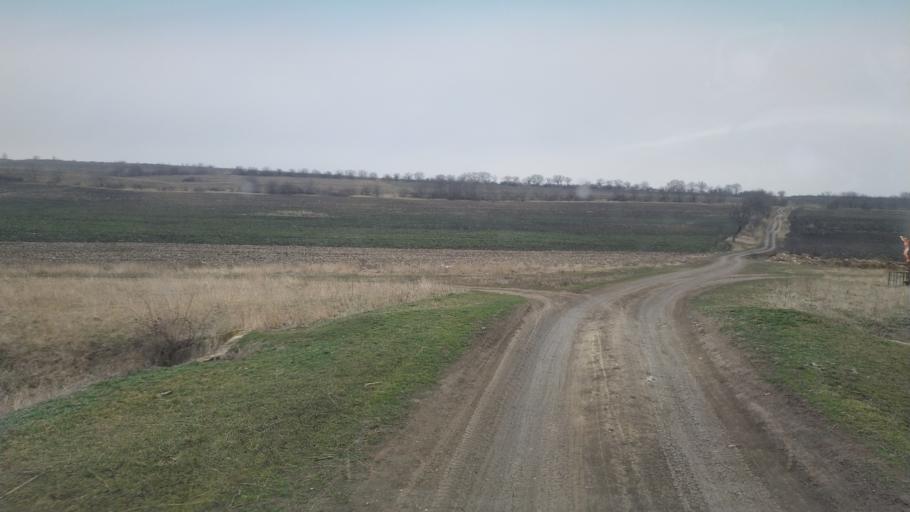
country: MD
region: Chisinau
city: Singera
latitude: 46.8270
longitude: 29.0118
